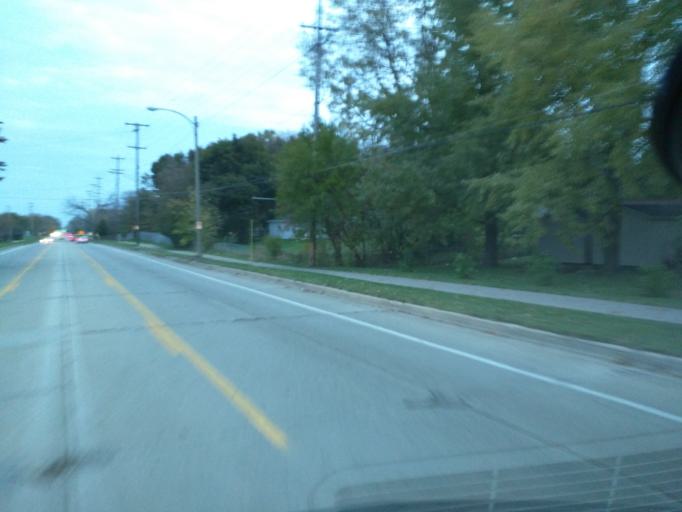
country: US
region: Michigan
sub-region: Eaton County
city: Waverly
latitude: 42.6867
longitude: -84.6031
